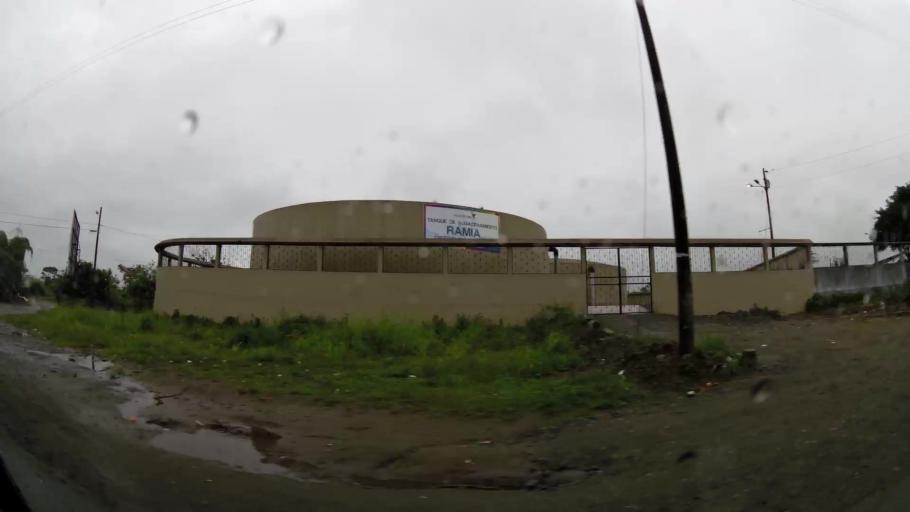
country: EC
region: Santo Domingo de los Tsachilas
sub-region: Canton Santo Domingo de los Colorados
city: Santo Domingo de los Colorados
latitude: -0.2330
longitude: -79.1590
